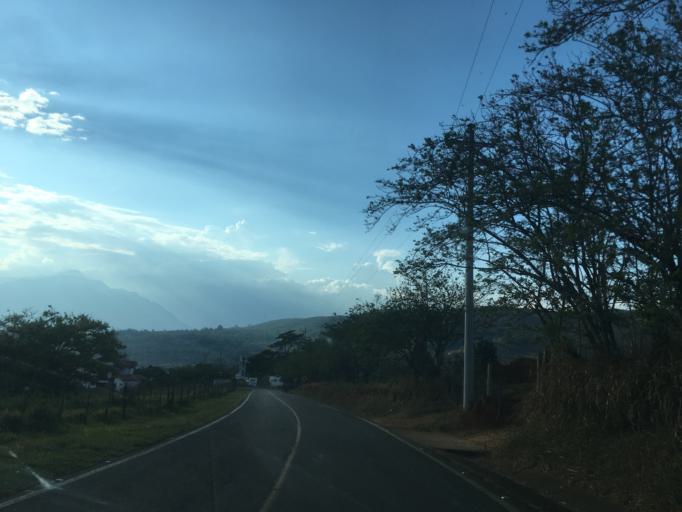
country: CO
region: Santander
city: Barichara
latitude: 6.6408
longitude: -73.1893
